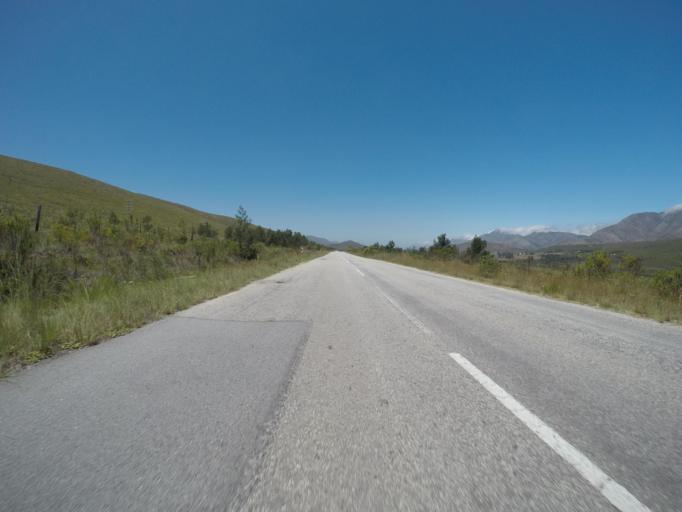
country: ZA
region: Eastern Cape
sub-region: Cacadu District Municipality
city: Kareedouw
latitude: -33.8484
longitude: 23.9626
